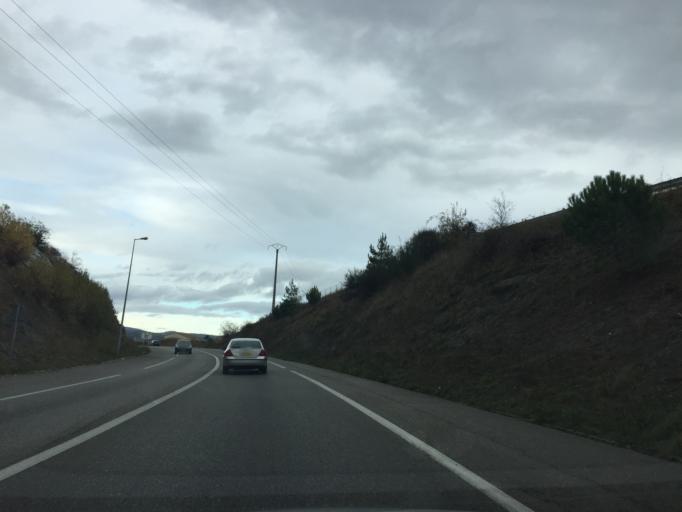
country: FR
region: Rhone-Alpes
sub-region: Departement de l'Ardeche
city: Saint-Etienne-de-Fontbellon
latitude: 44.5944
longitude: 4.3920
